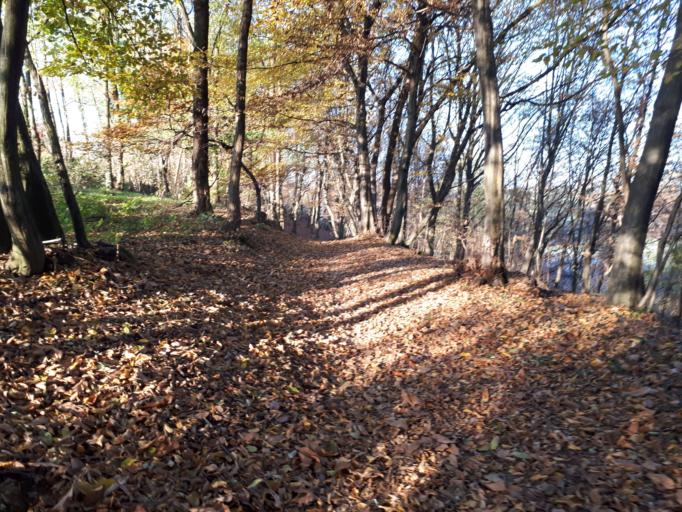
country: IT
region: Lombardy
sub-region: Provincia di Lecco
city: Quattro Strade
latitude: 45.6862
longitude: 9.3722
